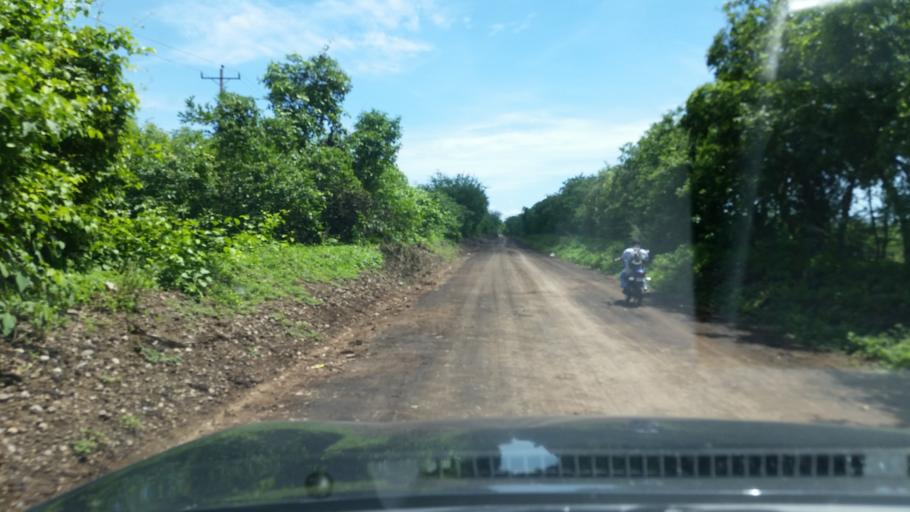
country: NI
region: Chinandega
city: El Viejo
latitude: 12.7553
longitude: -87.1336
